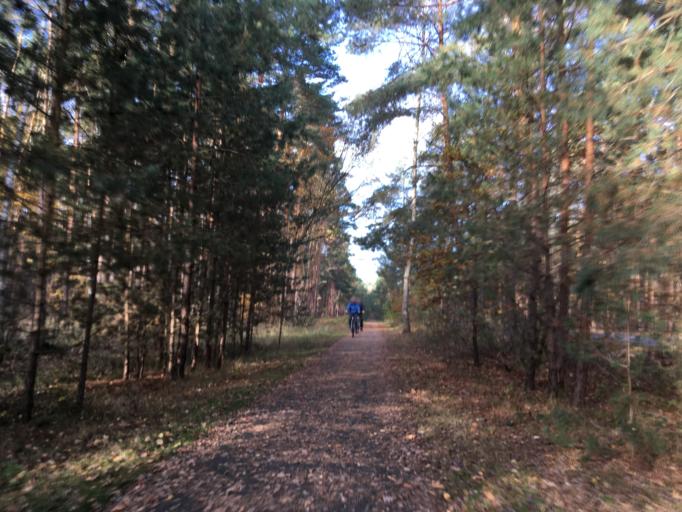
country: DE
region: Brandenburg
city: Gross Koris
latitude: 52.1576
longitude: 13.6723
